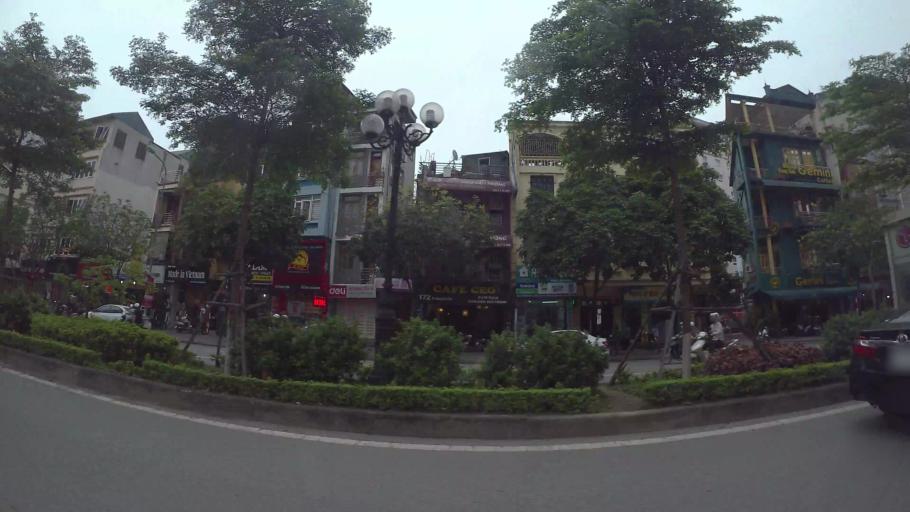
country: VN
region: Ha Noi
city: Cau Giay
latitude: 21.0207
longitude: 105.7916
